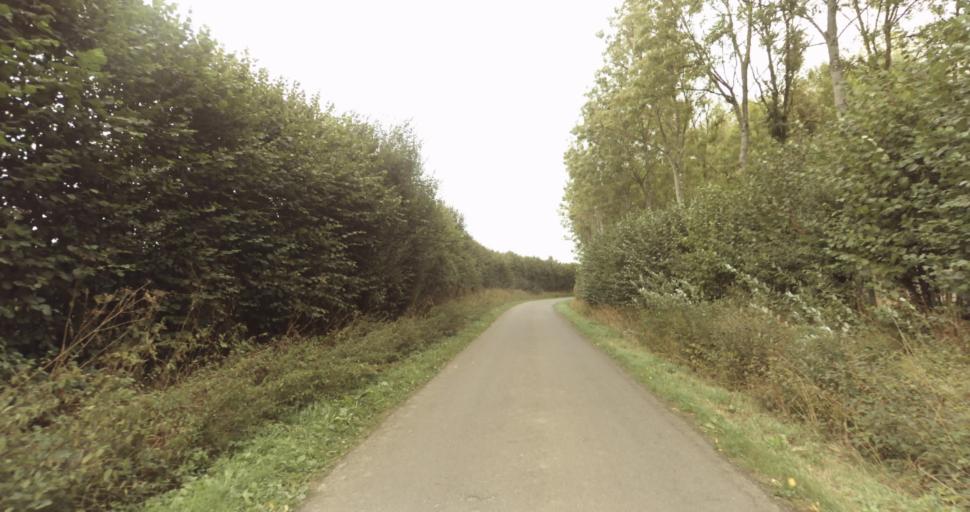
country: FR
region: Lower Normandy
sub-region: Departement de l'Orne
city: Gace
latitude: 48.8181
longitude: 0.3640
